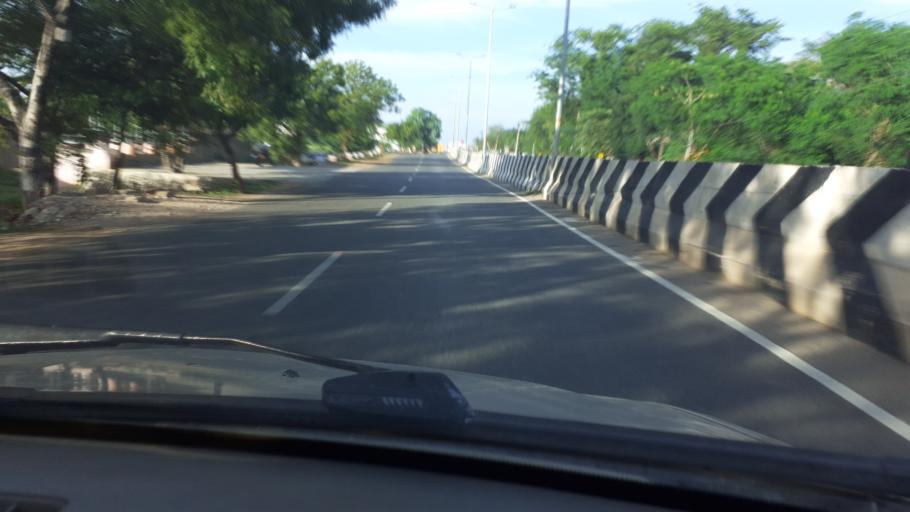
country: IN
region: Tamil Nadu
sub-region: Tirunelveli Kattabo
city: Tirunelveli
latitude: 8.6856
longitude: 77.7249
